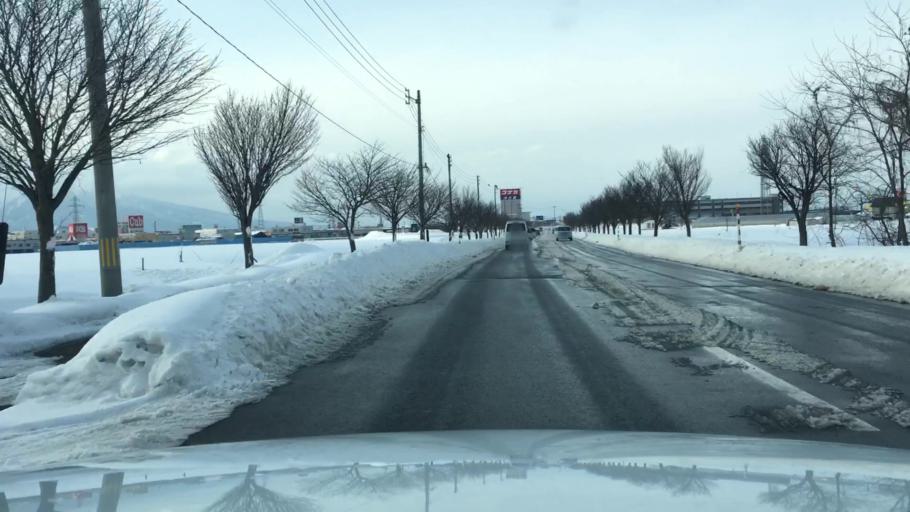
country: JP
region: Aomori
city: Hirosaki
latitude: 40.5953
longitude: 140.5177
